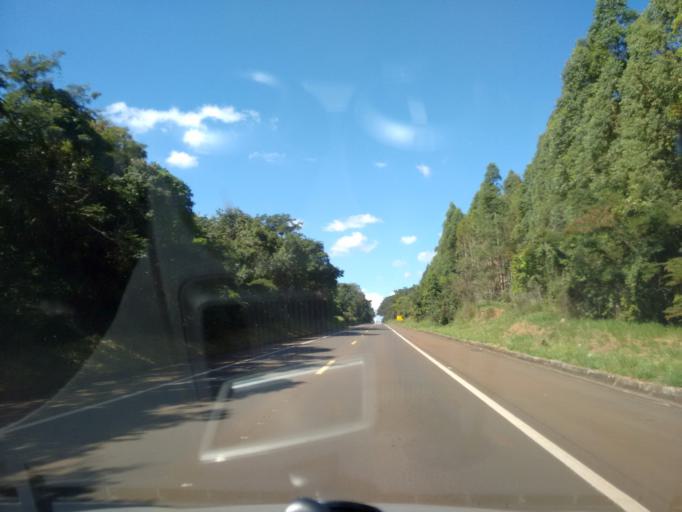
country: BR
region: Sao Paulo
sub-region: Ribeirao Bonito
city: Ribeirao Bonito
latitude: -22.0847
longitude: -48.1632
